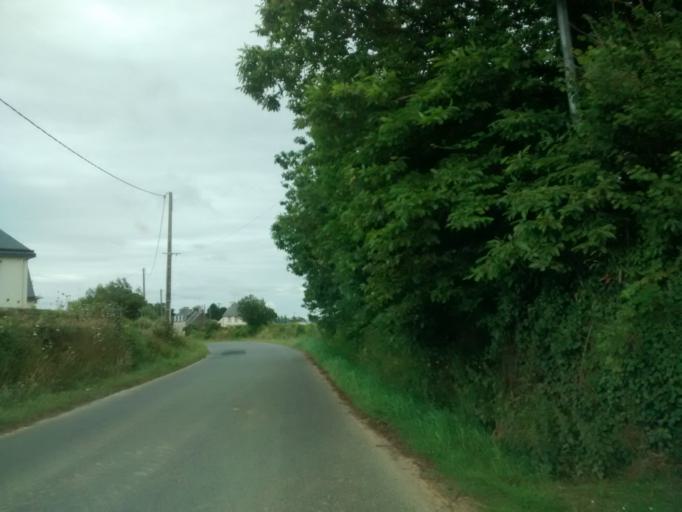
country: FR
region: Brittany
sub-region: Departement des Cotes-d'Armor
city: Trevou-Treguignec
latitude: 48.7864
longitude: -3.3362
